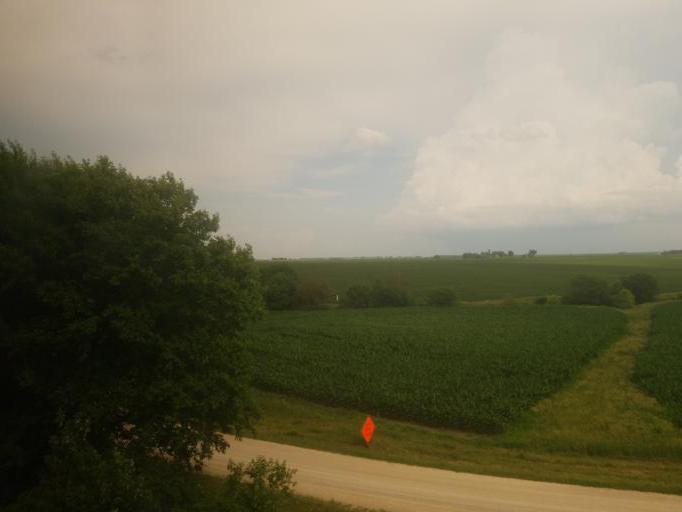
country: US
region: Illinois
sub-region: Henry County
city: Galva
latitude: 41.1342
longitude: -90.1158
